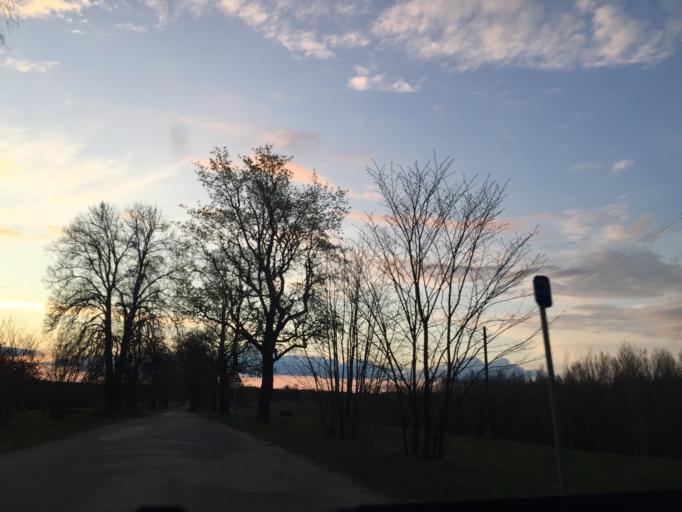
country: LV
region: Aluksnes Rajons
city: Aluksne
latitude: 57.2767
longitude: 26.9245
